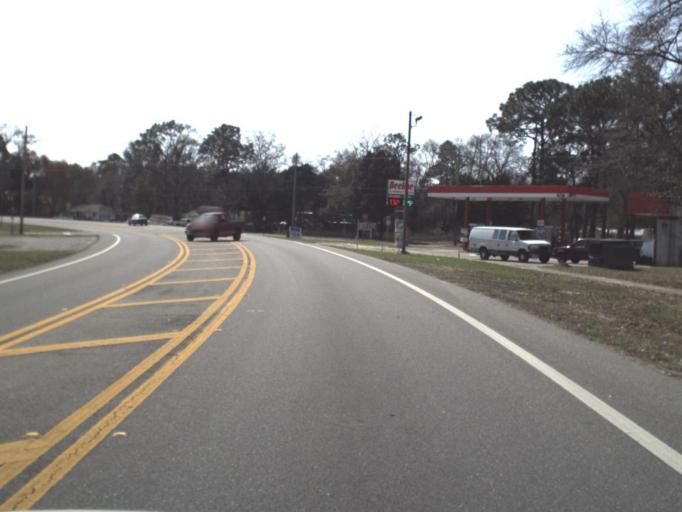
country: US
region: Florida
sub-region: Bay County
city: Lynn Haven
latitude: 30.2369
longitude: -85.6548
